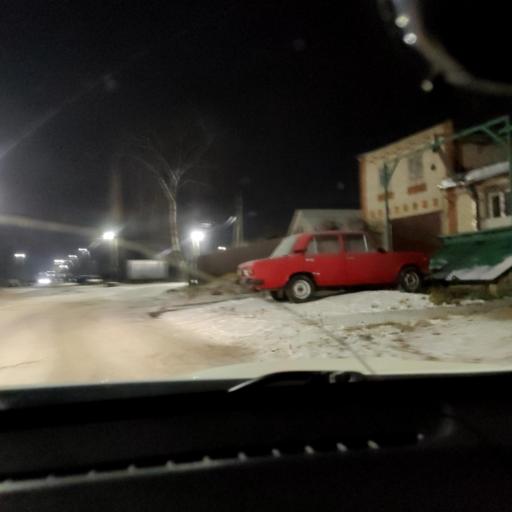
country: RU
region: Tatarstan
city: Staroye Arakchino
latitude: 55.8725
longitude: 49.0510
